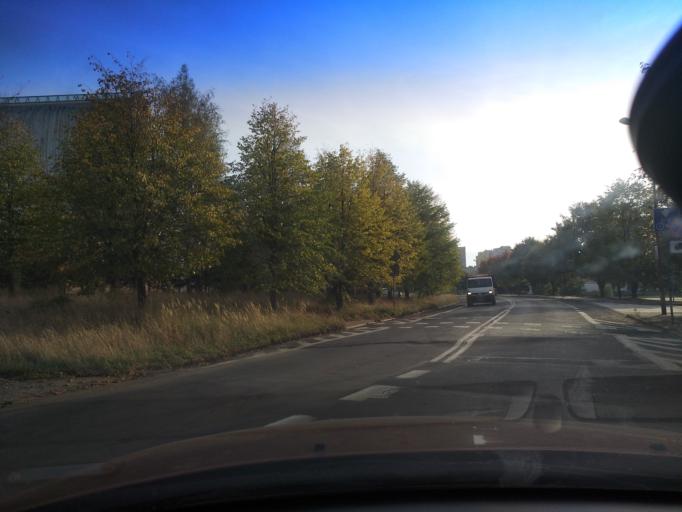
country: PL
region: Lower Silesian Voivodeship
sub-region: Powiat zgorzelecki
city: Zgorzelec
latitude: 51.1618
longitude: 15.0090
